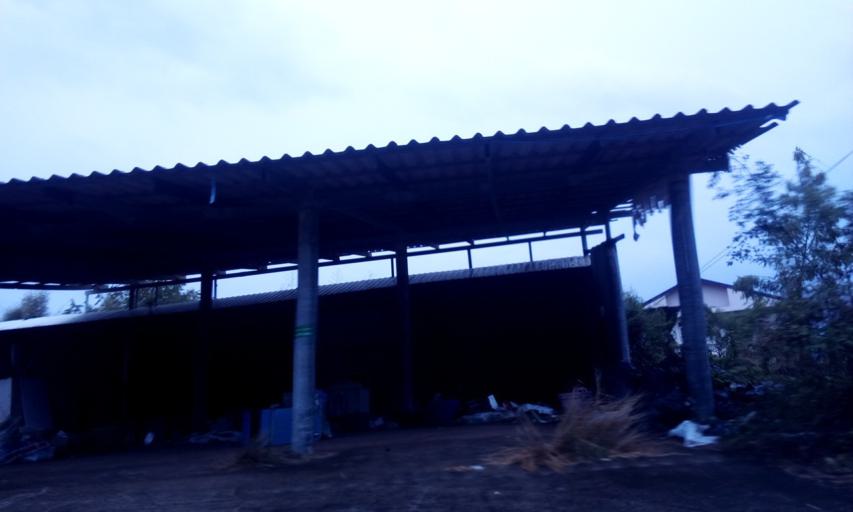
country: TH
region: Trat
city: Laem Ngop
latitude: 12.2159
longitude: 102.2995
